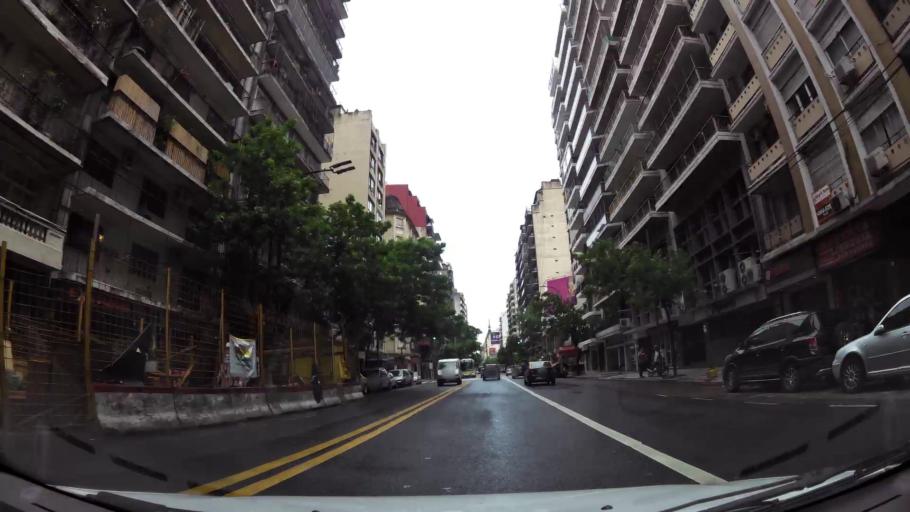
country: AR
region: Buenos Aires F.D.
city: Retiro
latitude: -34.5995
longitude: -58.4041
